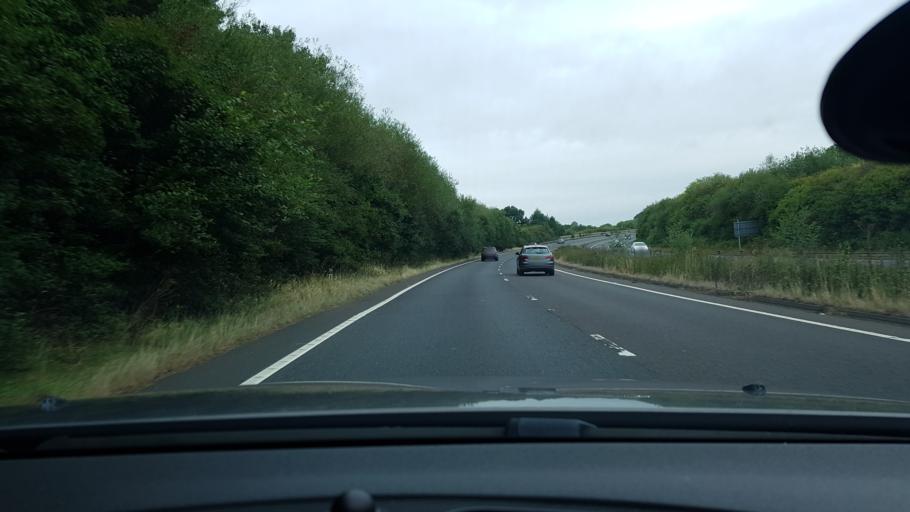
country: GB
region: England
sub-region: Hampshire
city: Highclere
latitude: 51.3653
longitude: -1.3621
